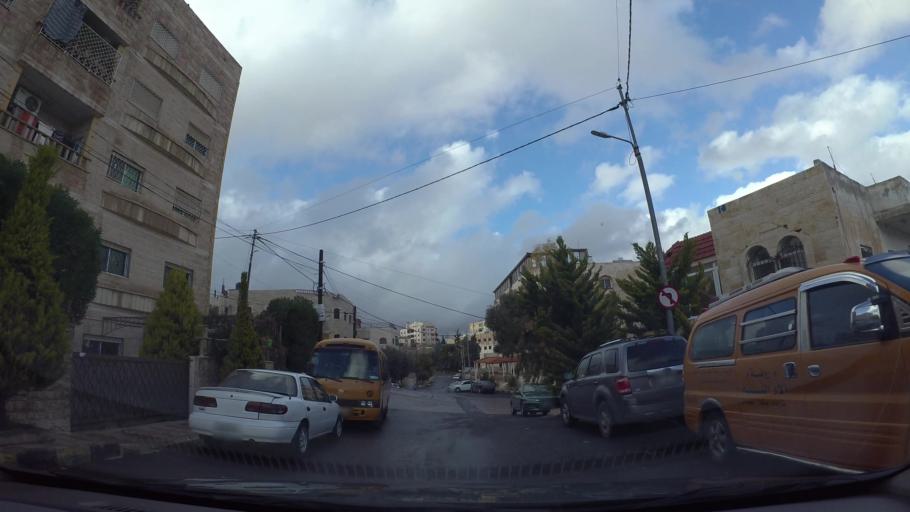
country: JO
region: Amman
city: Amman
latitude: 32.0022
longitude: 35.9217
